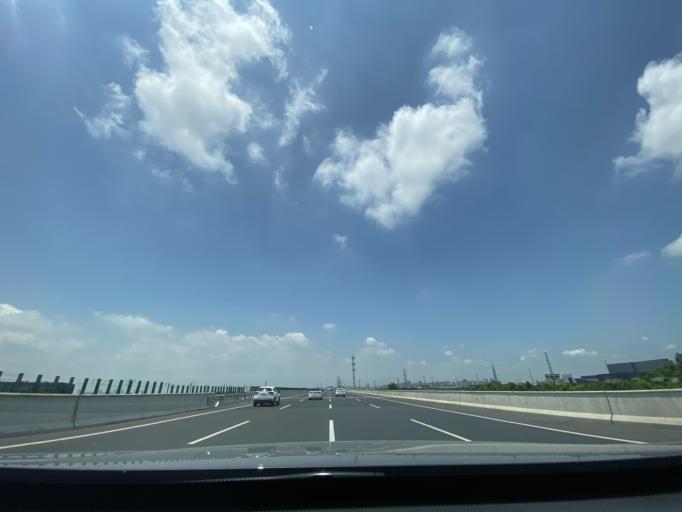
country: CN
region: Sichuan
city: Longquan
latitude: 30.5436
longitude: 104.1546
